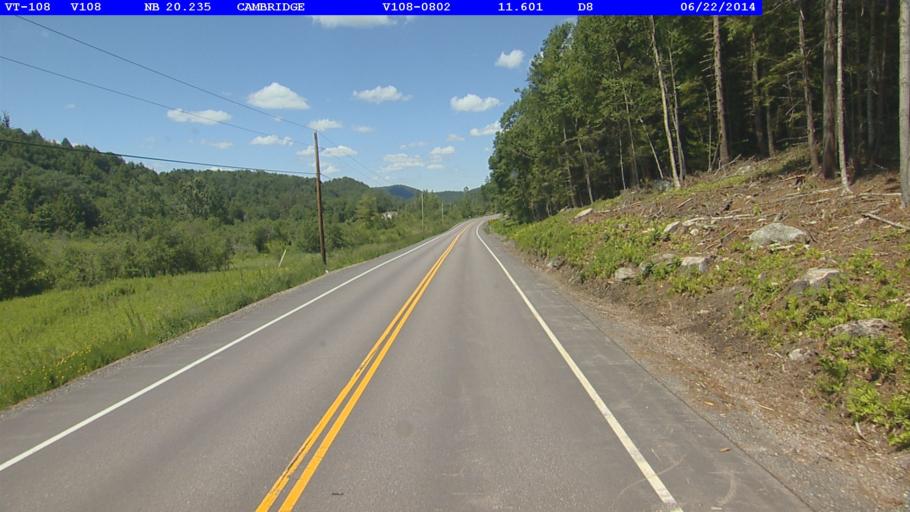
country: US
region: Vermont
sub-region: Lamoille County
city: Johnson
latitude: 44.6824
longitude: -72.8253
